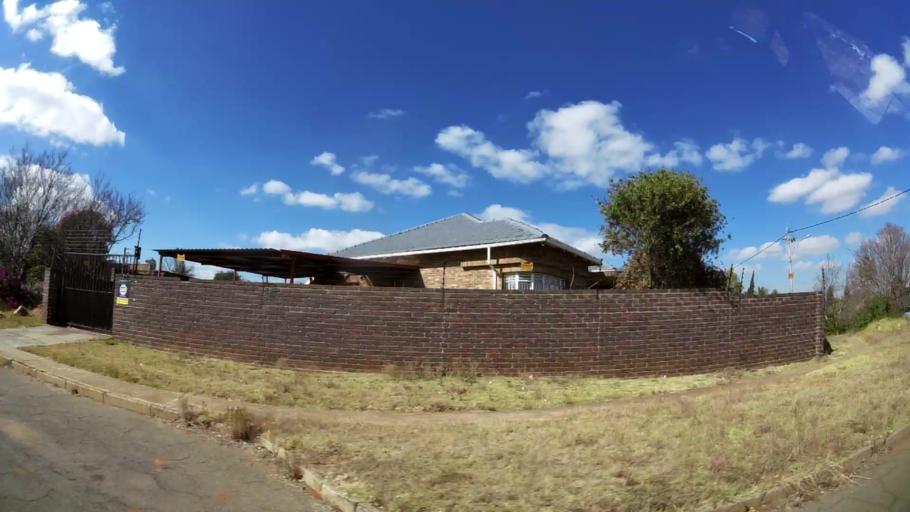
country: ZA
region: Gauteng
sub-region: West Rand District Municipality
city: Krugersdorp
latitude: -26.0940
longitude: 27.7831
